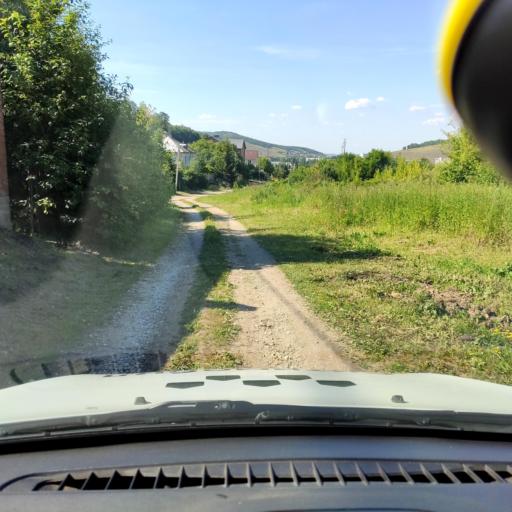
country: RU
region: Samara
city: Zhigulevsk
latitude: 53.3926
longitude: 49.5301
